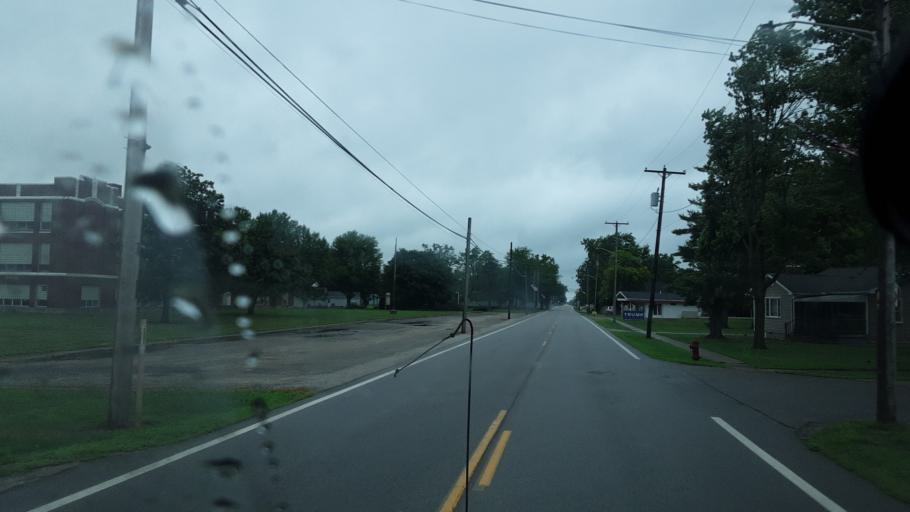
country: US
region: Ohio
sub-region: Mercer County
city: Rockford
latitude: 40.7683
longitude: -84.6229
